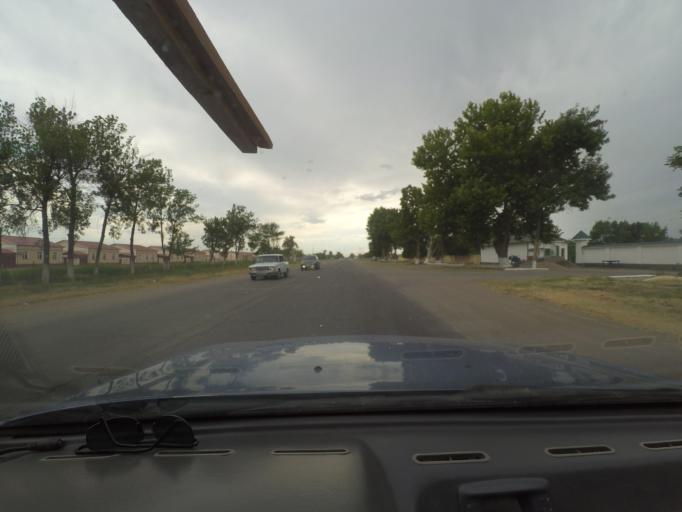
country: UZ
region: Sirdaryo
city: Guliston
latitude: 40.4926
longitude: 68.8272
